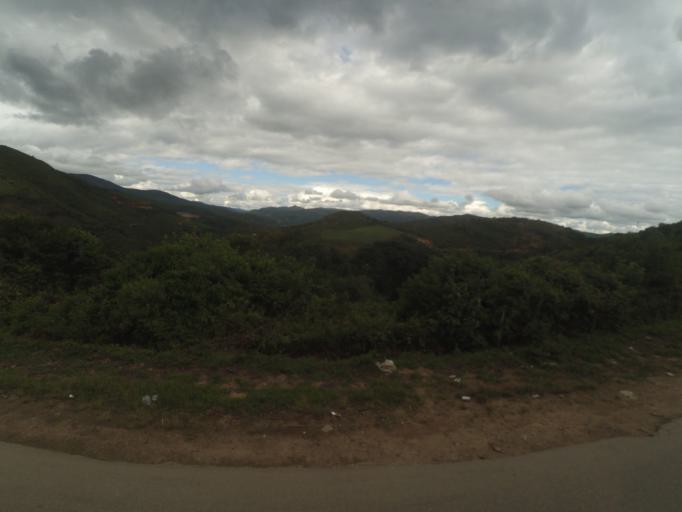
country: BO
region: Santa Cruz
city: Samaipata
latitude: -18.1752
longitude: -63.8572
